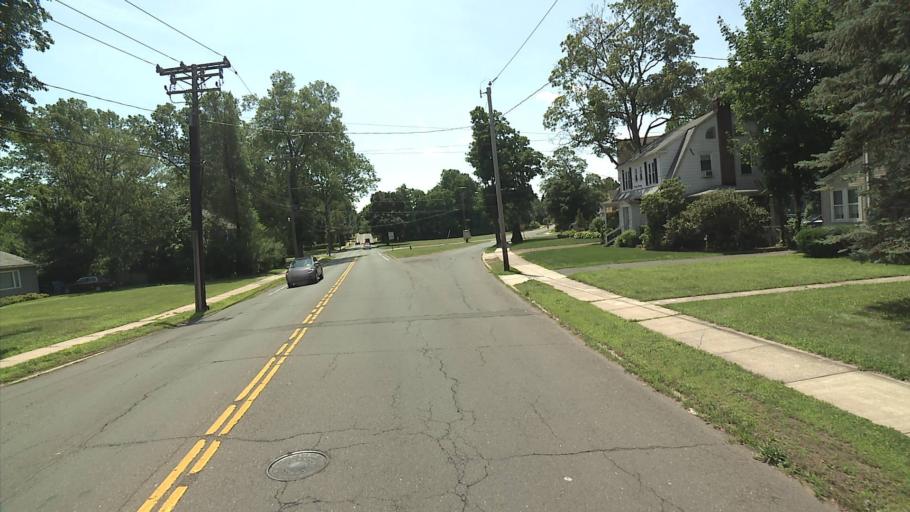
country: US
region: Connecticut
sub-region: Hartford County
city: New Britain
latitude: 41.6559
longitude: -72.7980
